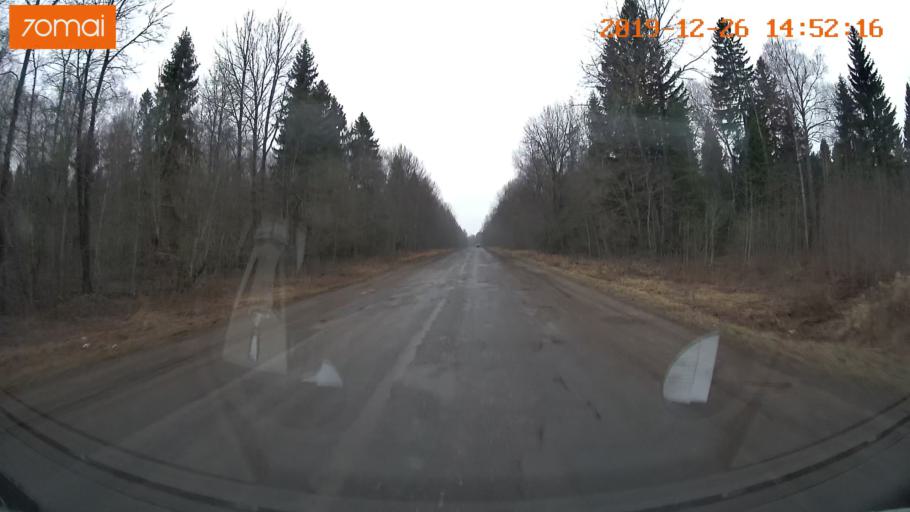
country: RU
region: Jaroslavl
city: Rybinsk
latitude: 58.3226
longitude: 38.9003
